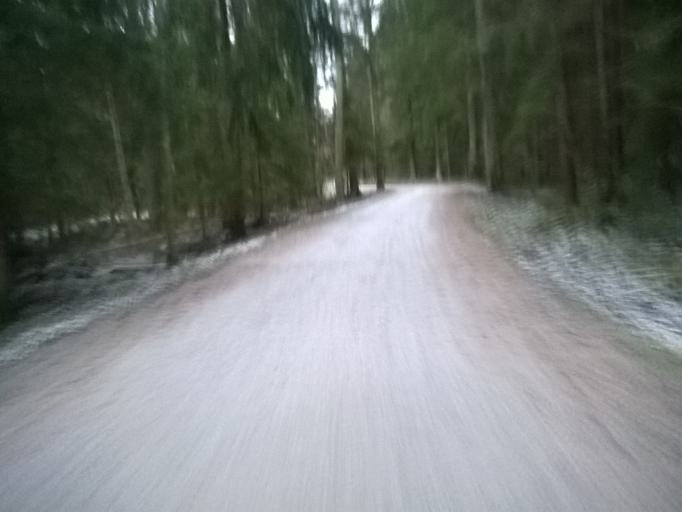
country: FI
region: Uusimaa
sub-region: Helsinki
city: Helsinki
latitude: 60.2548
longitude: 24.9033
